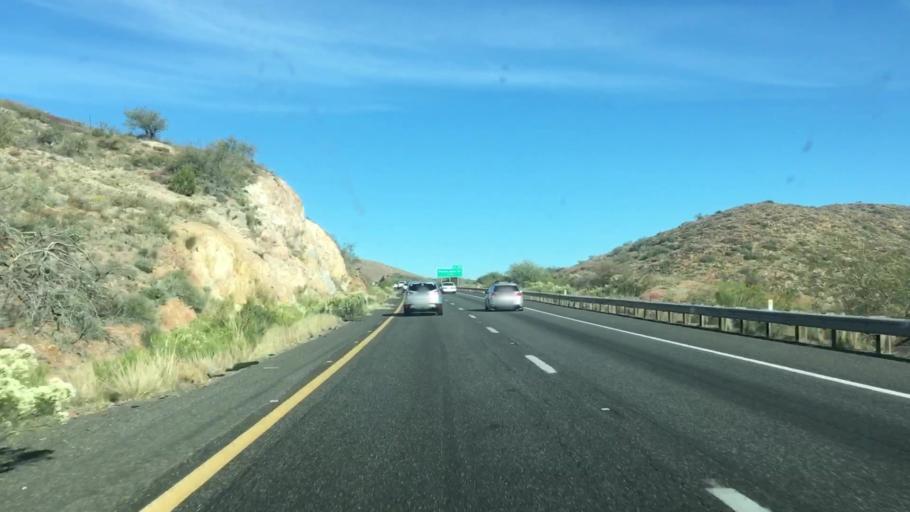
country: US
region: Arizona
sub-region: Yavapai County
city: Cordes Lakes
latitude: 34.2666
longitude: -112.1113
